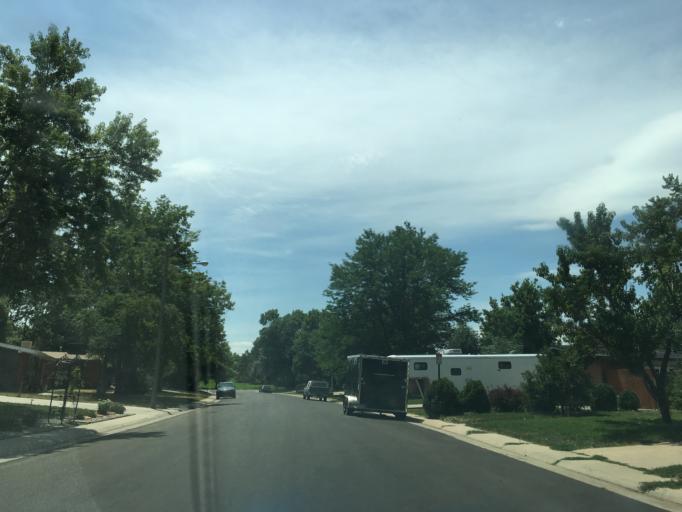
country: US
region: Colorado
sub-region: Arapahoe County
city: Sheridan
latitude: 39.6809
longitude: -105.0453
